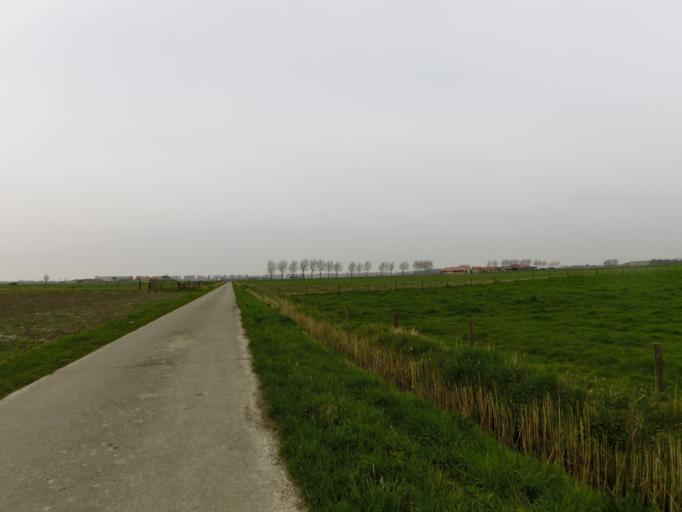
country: BE
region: Flanders
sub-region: Provincie West-Vlaanderen
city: Middelkerke
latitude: 51.1609
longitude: 2.8192
